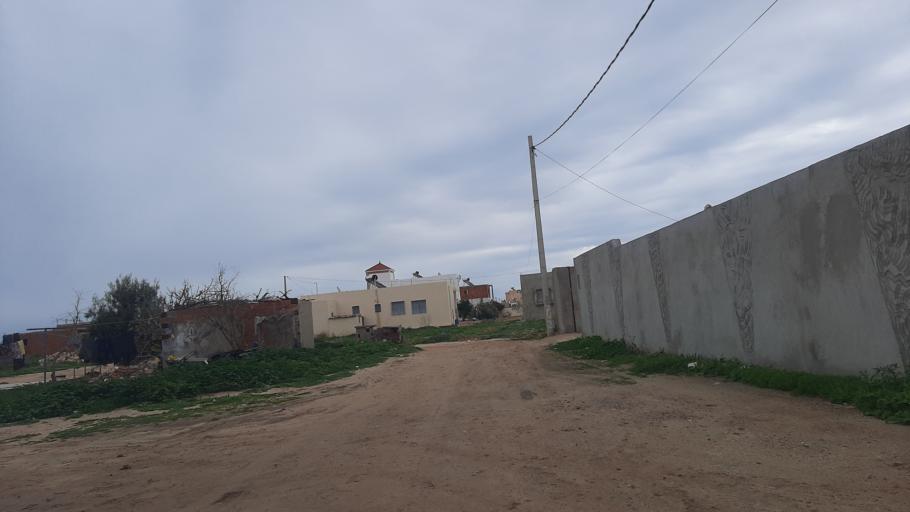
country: TN
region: Safaqis
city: Al Qarmadah
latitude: 34.7989
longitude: 10.8542
